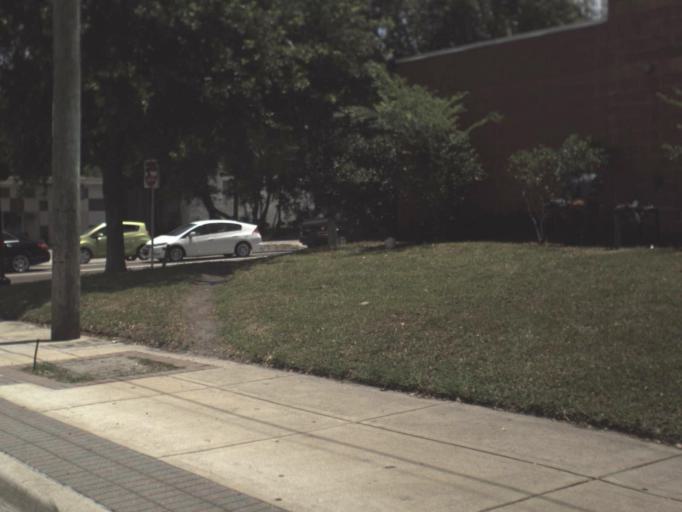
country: US
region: Florida
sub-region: Duval County
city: Jacksonville
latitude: 30.3338
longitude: -81.6639
